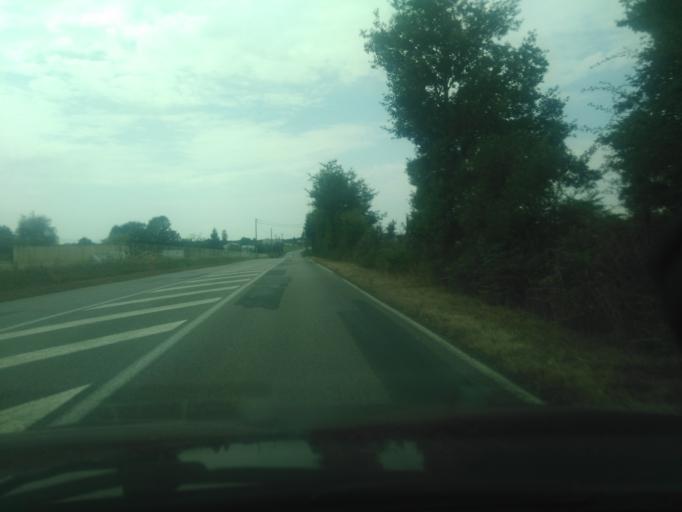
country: FR
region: Poitou-Charentes
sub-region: Departement des Deux-Sevres
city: Secondigny
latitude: 46.6316
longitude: -0.5032
